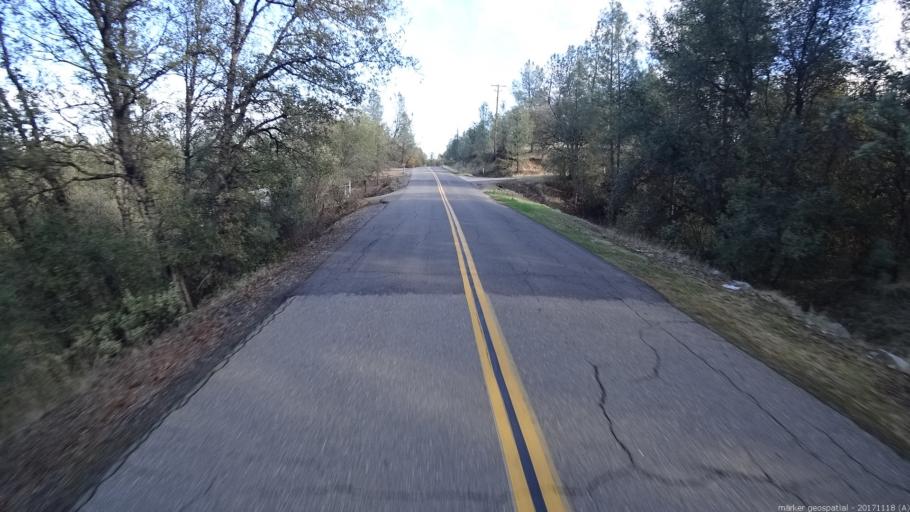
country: US
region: California
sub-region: Shasta County
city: Anderson
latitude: 40.4726
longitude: -122.4047
